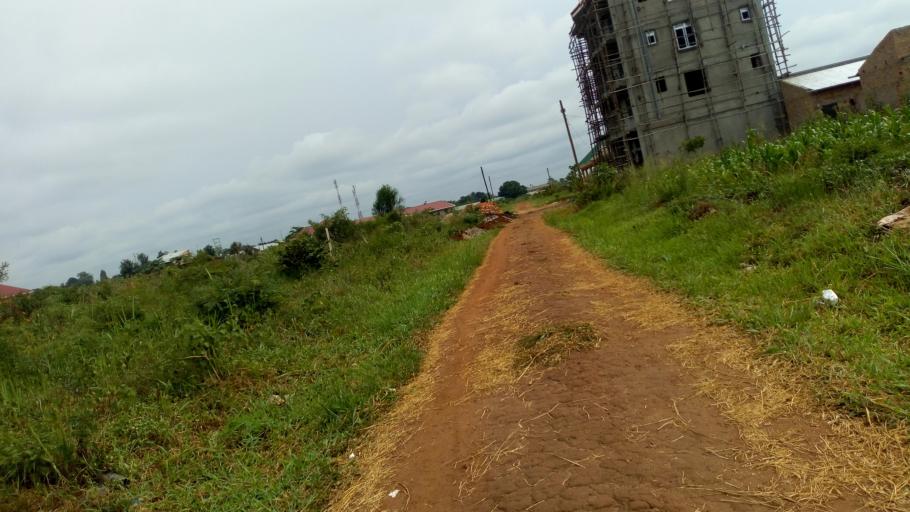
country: UG
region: Western Region
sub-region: Kiryandongo District
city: Kiryandongo
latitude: 1.8020
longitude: 32.0137
